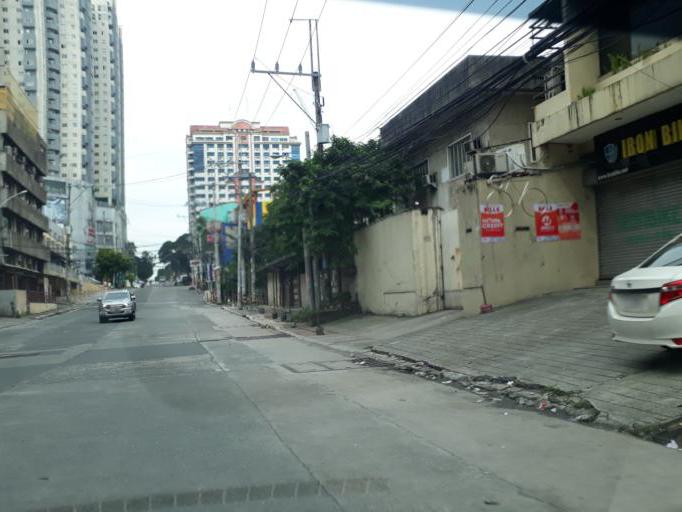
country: PH
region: Calabarzon
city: Del Monte
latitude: 14.6373
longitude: 121.0291
